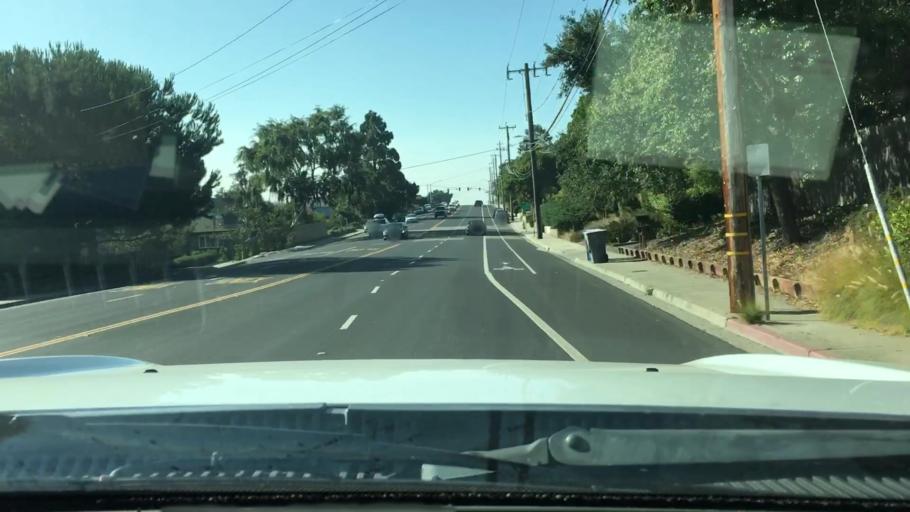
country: US
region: California
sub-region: San Luis Obispo County
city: San Luis Obispo
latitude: 35.2719
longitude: -120.6441
